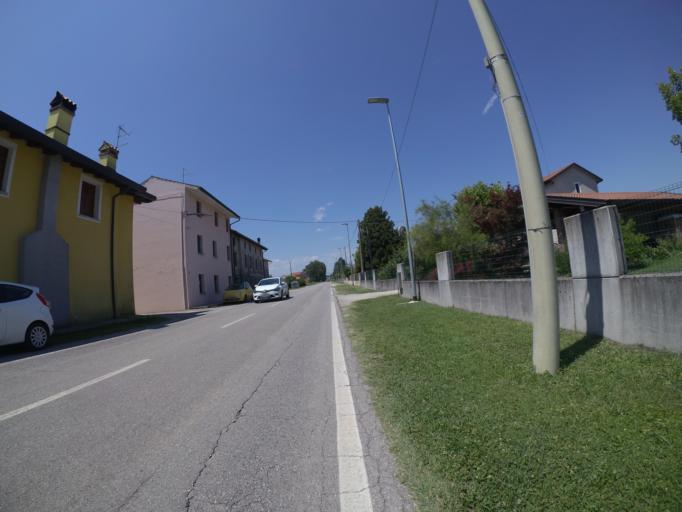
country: IT
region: Friuli Venezia Giulia
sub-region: Provincia di Udine
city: Talmassons
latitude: 45.9239
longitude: 13.1342
